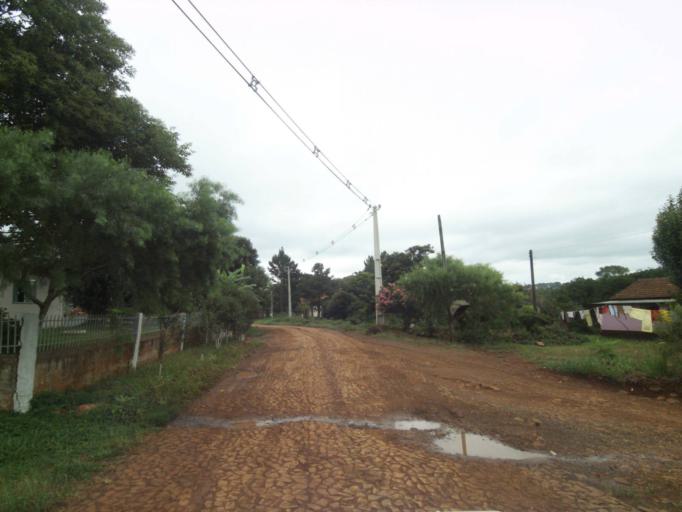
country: BR
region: Parana
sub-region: Pitanga
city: Pitanga
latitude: -24.9293
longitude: -51.8710
